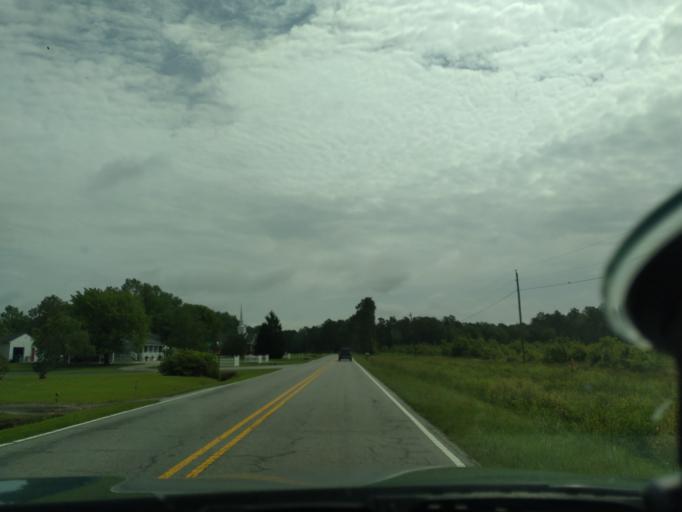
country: US
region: North Carolina
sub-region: Washington County
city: Plymouth
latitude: 35.8938
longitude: -76.6994
